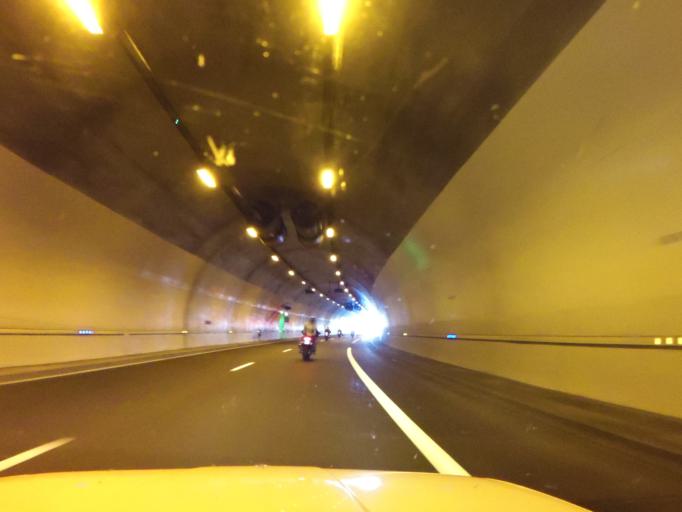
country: FR
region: Languedoc-Roussillon
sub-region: Departement de l'Herault
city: Lodeve
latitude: 43.8309
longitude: 3.3127
